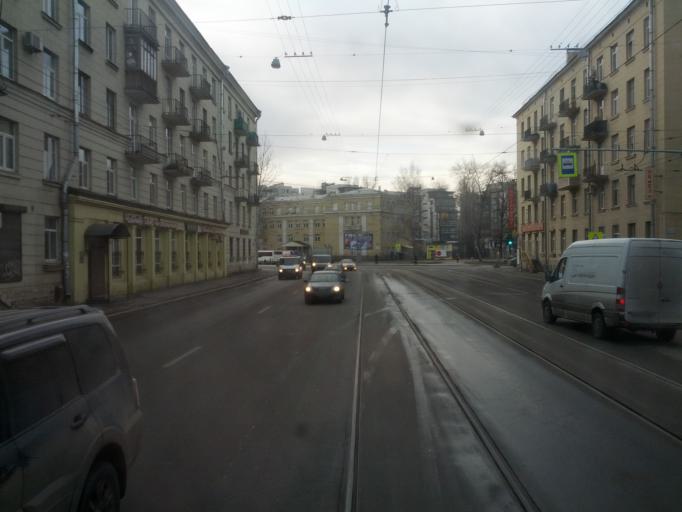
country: RU
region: St.-Petersburg
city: Centralniy
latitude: 59.9346
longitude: 30.4074
